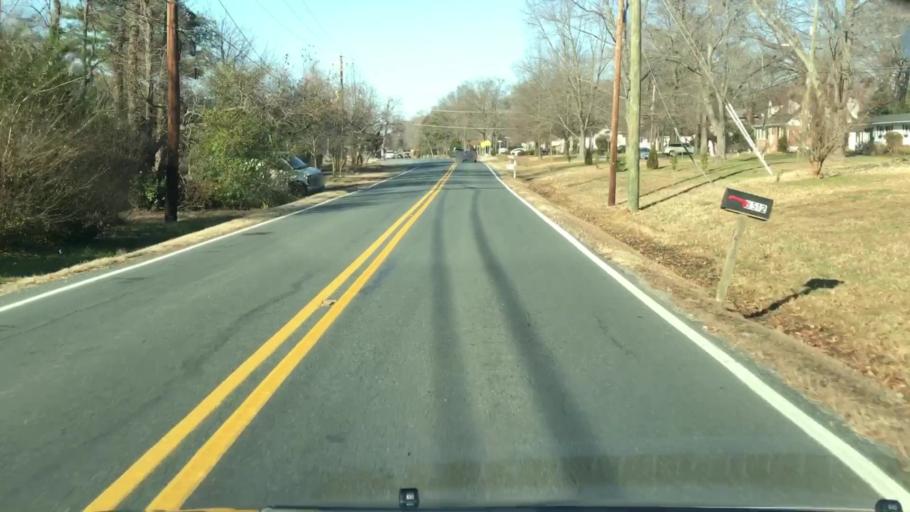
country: US
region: Virginia
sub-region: Fairfax County
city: Mount Vernon
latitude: 38.7263
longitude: -77.0908
